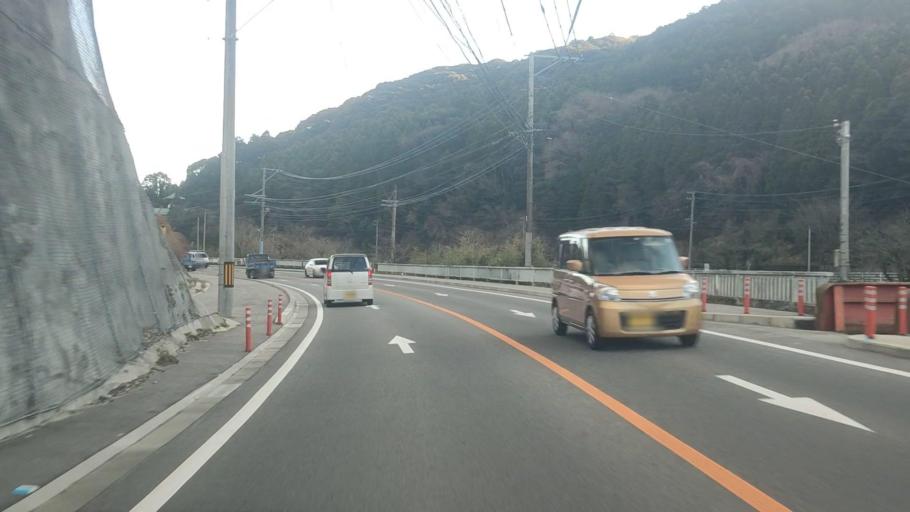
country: JP
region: Saga Prefecture
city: Saga-shi
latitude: 33.3330
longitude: 130.2630
